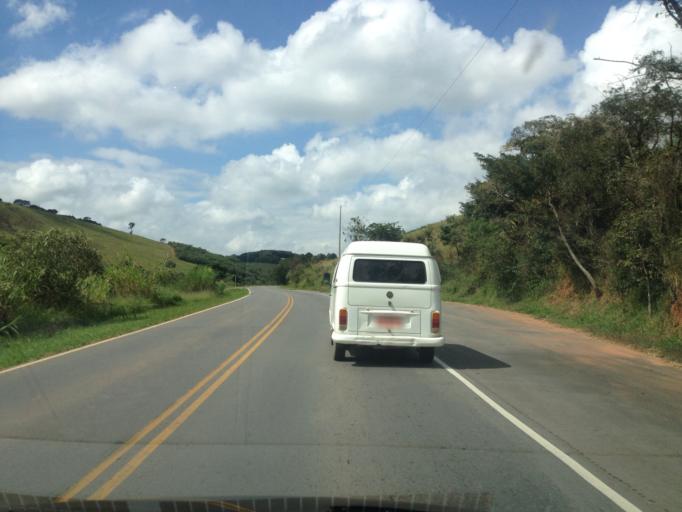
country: BR
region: Minas Gerais
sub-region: Itanhandu
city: Itanhandu
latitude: -22.2057
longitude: -44.9579
